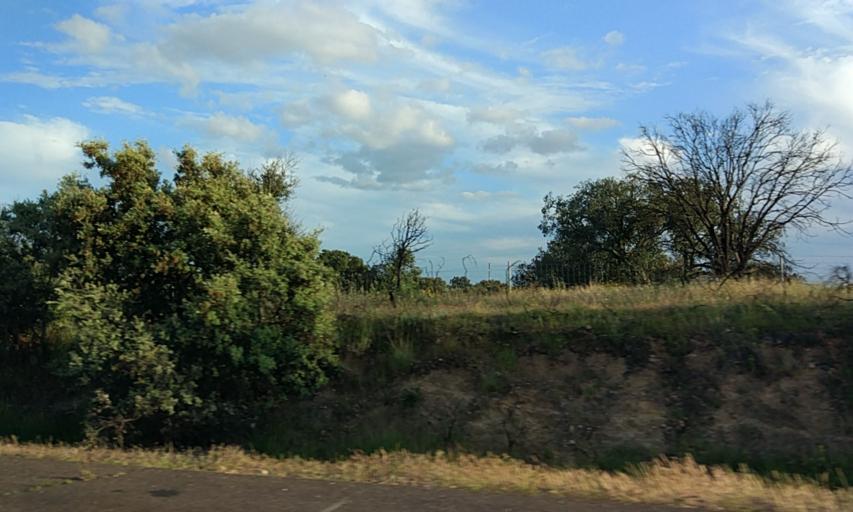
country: ES
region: Extremadura
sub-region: Provincia de Badajoz
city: Talavera La Real
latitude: 38.8709
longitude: -6.8566
